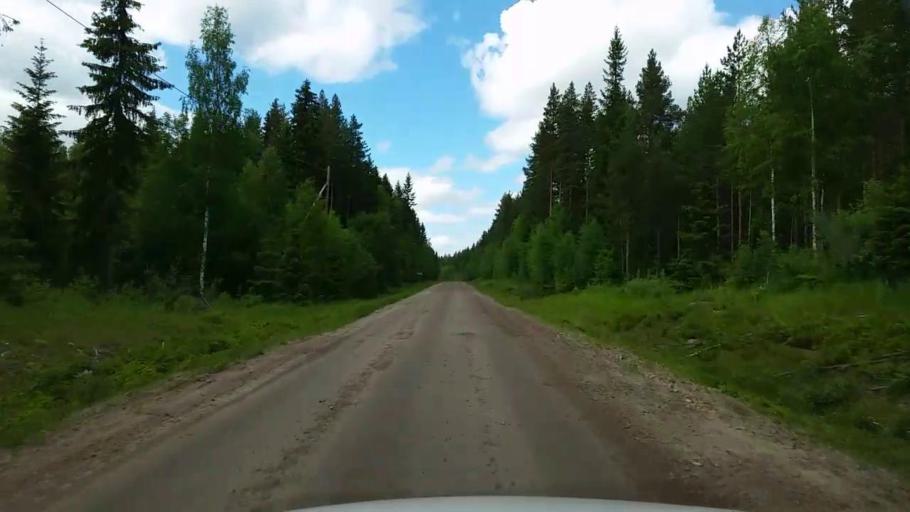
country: SE
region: Gaevleborg
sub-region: Ovanakers Kommun
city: Alfta
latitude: 61.4911
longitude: 15.9844
